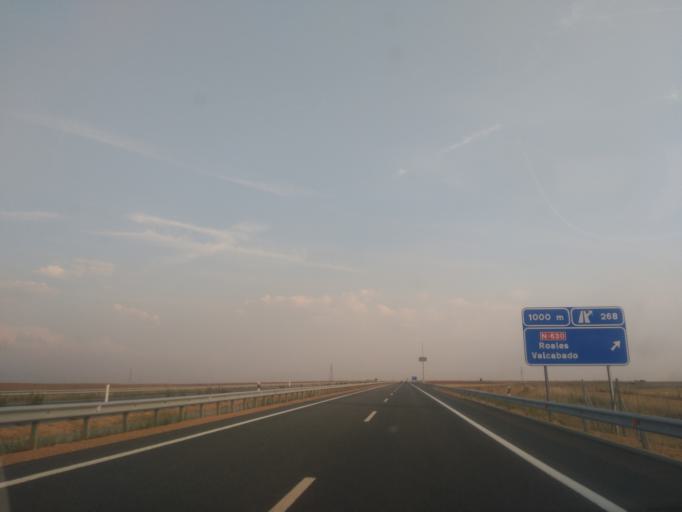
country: ES
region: Castille and Leon
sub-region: Provincia de Zamora
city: Roales
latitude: 41.5905
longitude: -5.7794
